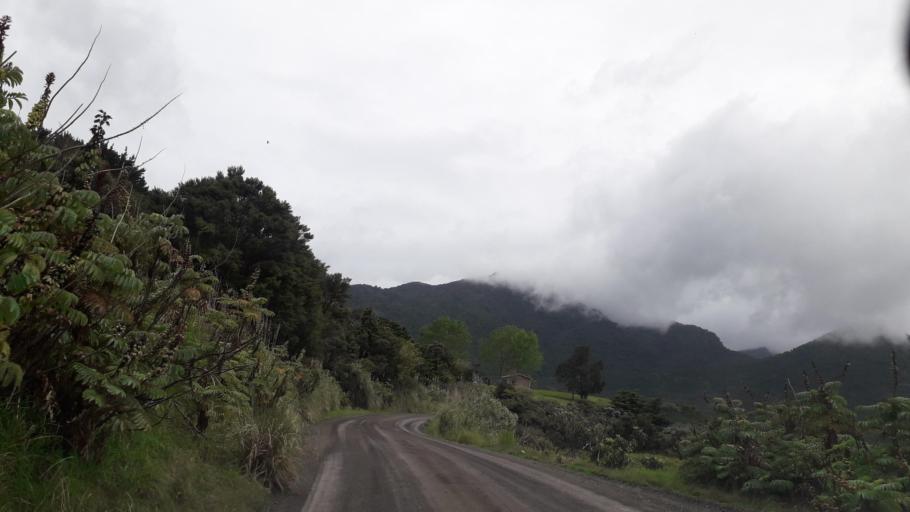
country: NZ
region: Northland
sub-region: Far North District
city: Kaitaia
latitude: -35.4124
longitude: 173.3654
